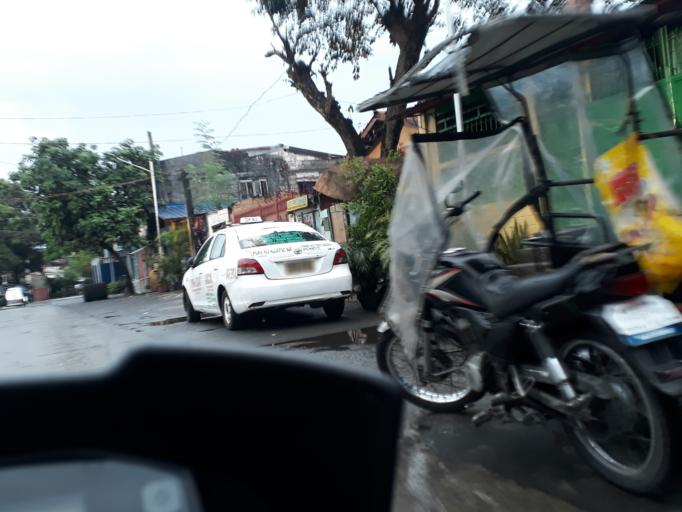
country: PH
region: Central Luzon
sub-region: Province of Bulacan
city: San Jose del Monte
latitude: 14.7747
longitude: 121.0498
